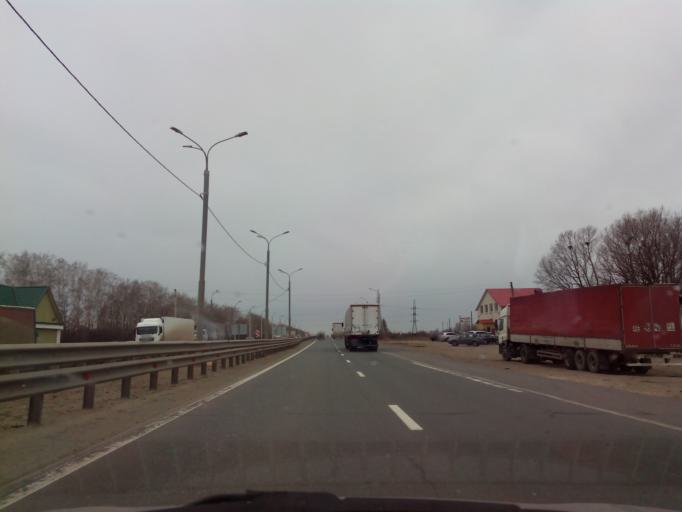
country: RU
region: Tambov
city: Komsomolets
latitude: 52.7347
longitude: 41.2839
